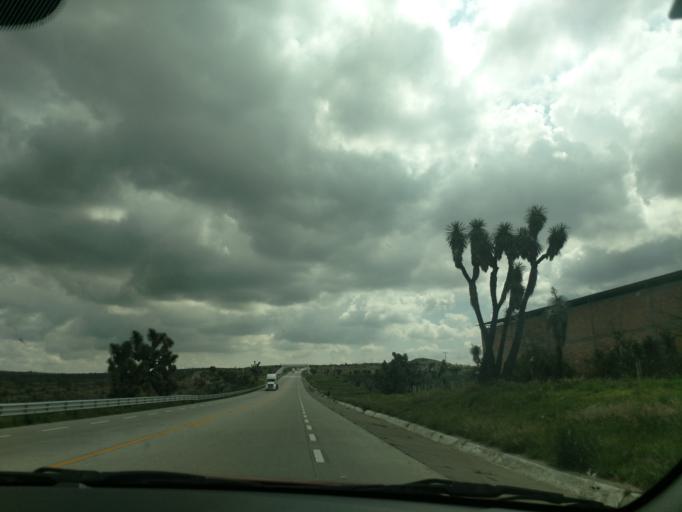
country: MX
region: Jalisco
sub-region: Ojuelos de Jalisco
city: Matanzas
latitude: 21.5655
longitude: -101.6809
